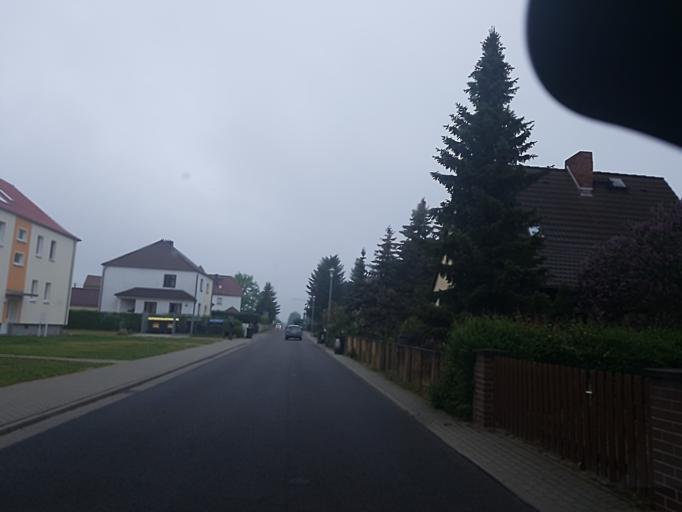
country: DE
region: Saxony-Anhalt
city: Jessen
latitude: 51.7997
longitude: 12.9561
